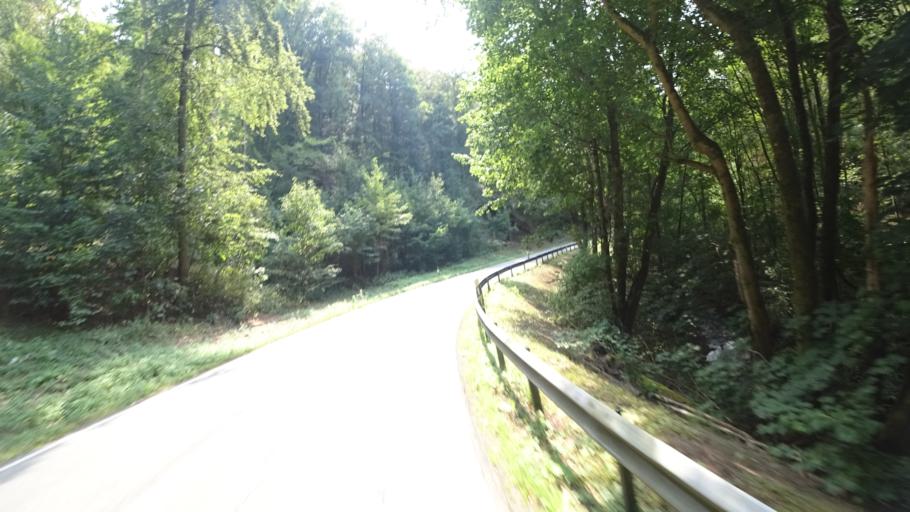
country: DE
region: Rheinland-Pfalz
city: Hohr-Grenzhausen
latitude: 50.4220
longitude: 7.6450
